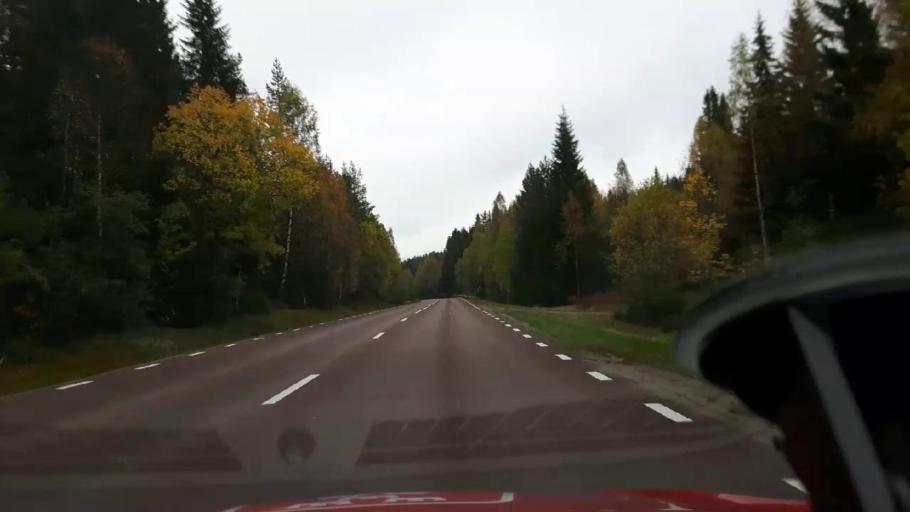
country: SE
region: Jaemtland
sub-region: Harjedalens Kommun
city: Sveg
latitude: 62.3382
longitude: 14.7284
